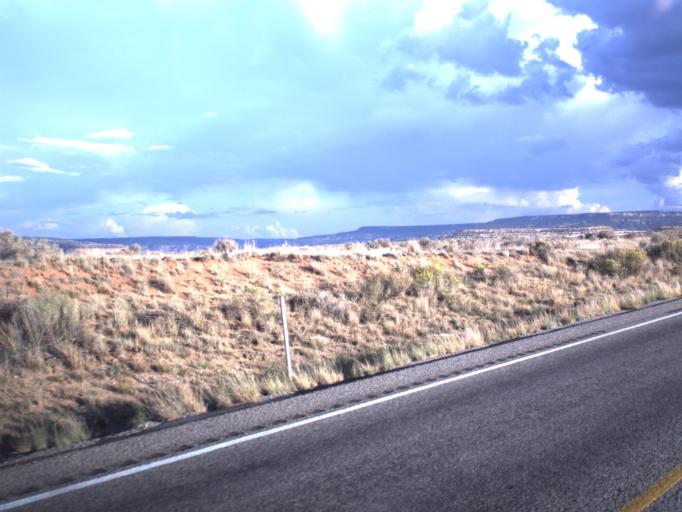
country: US
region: Utah
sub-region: San Juan County
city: Monticello
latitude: 38.1439
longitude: -109.3724
